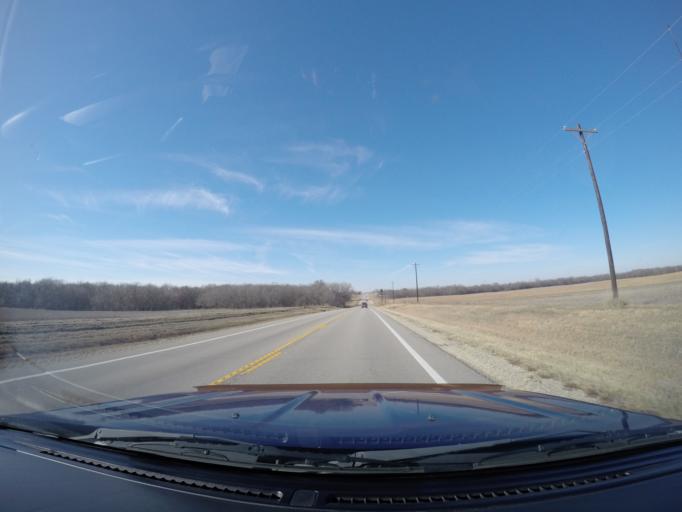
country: US
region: Kansas
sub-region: Clay County
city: Clay Center
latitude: 39.3796
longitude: -97.2285
